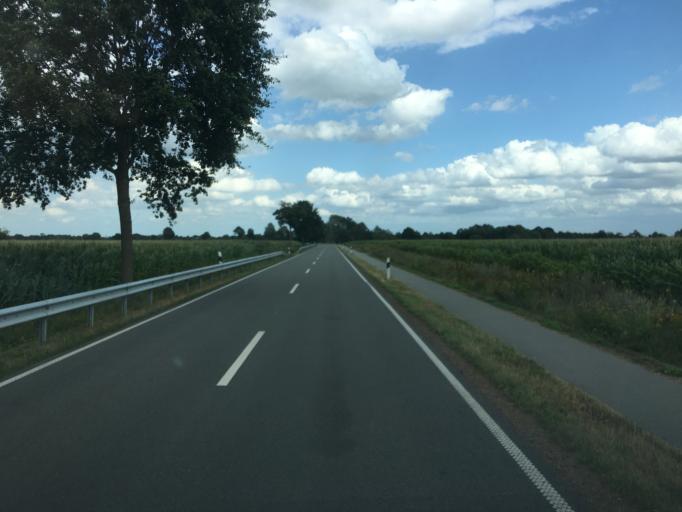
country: DE
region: Lower Saxony
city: Barssel
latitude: 53.0820
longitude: 7.7757
